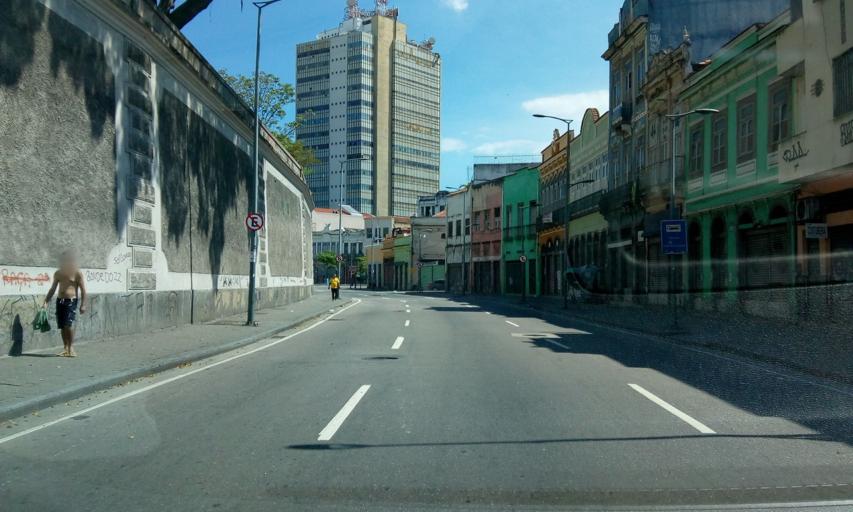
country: BR
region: Rio de Janeiro
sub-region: Rio De Janeiro
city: Rio de Janeiro
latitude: -22.8980
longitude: -43.1876
